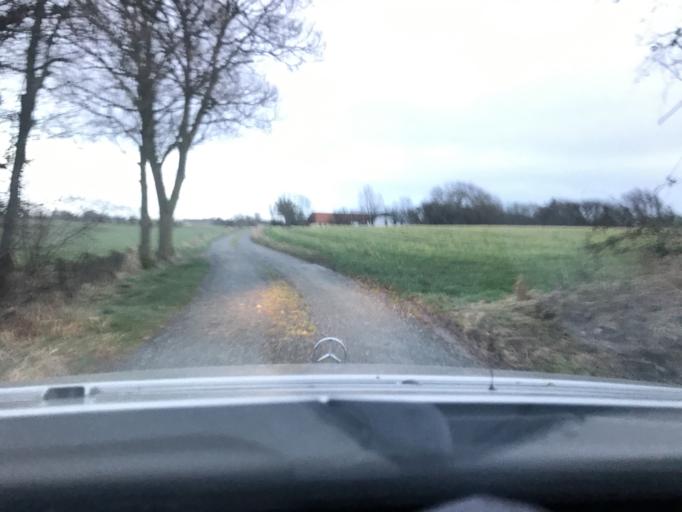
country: DK
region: South Denmark
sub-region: Sonderborg Kommune
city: Nordborg
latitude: 55.0706
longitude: 9.6913
